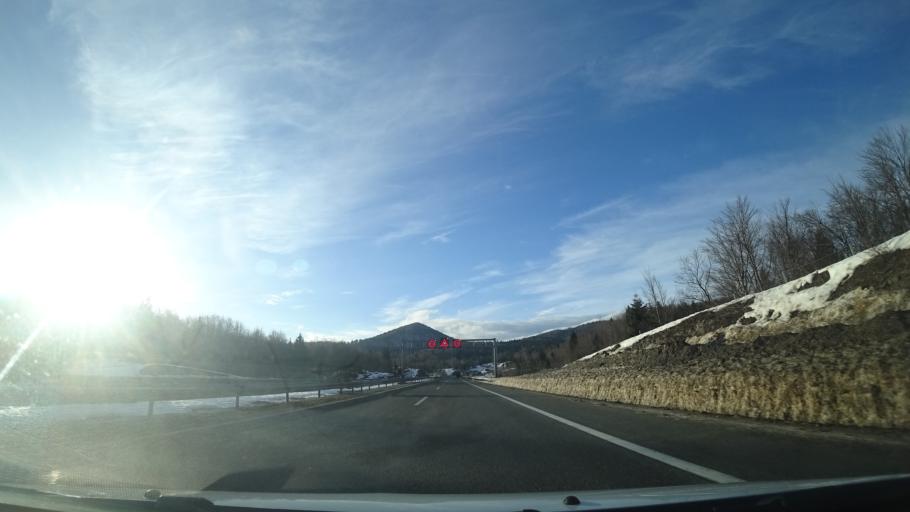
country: HR
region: Karlovacka
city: Ostarije
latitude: 45.1214
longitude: 15.2442
